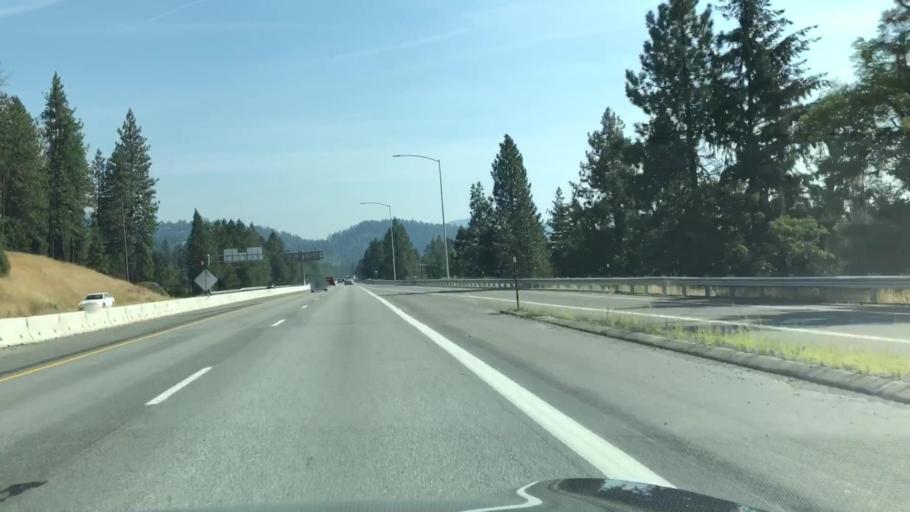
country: US
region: Idaho
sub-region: Kootenai County
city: Coeur d'Alene
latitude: 47.6852
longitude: -116.7616
